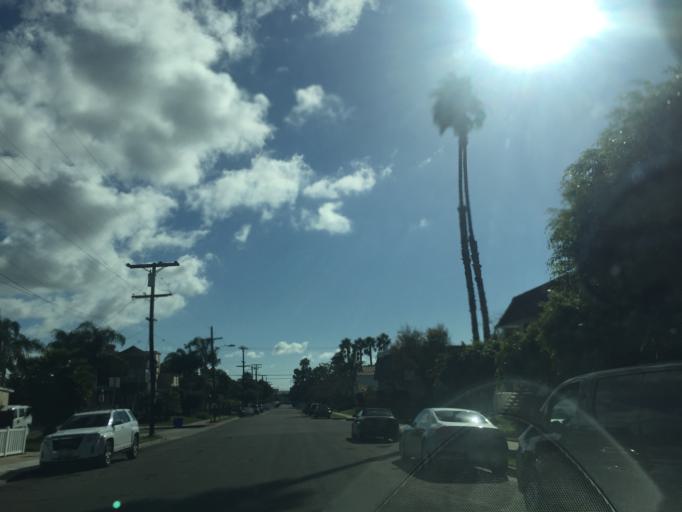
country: US
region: California
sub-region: San Diego County
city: La Jolla
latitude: 32.7947
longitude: -117.2432
